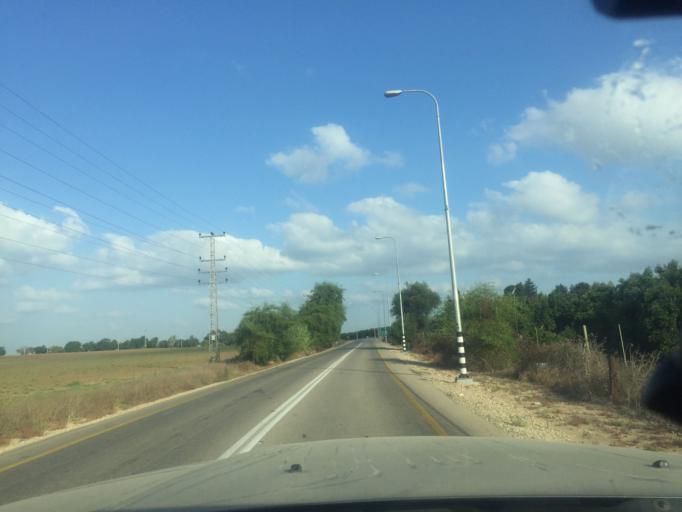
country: PS
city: Umm an Nasr
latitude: 31.6078
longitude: 34.5496
